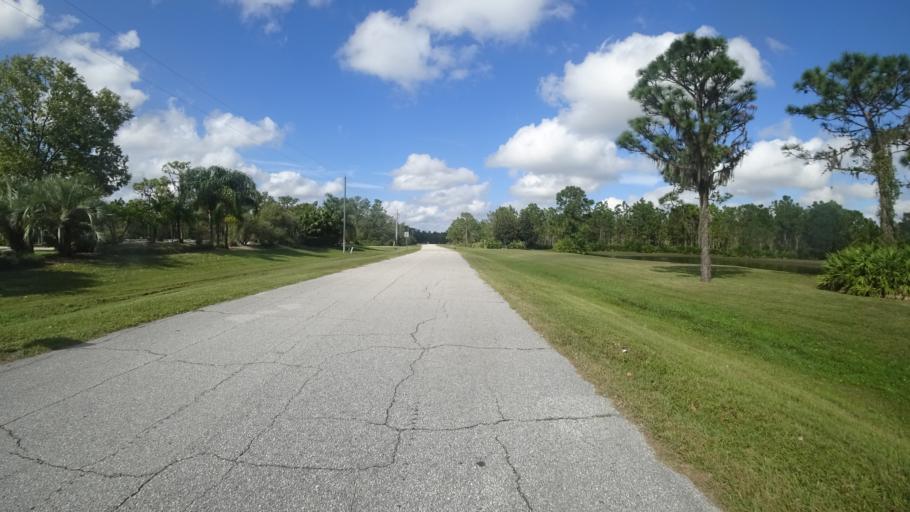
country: US
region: Florida
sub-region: Sarasota County
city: The Meadows
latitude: 27.3983
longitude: -82.3354
